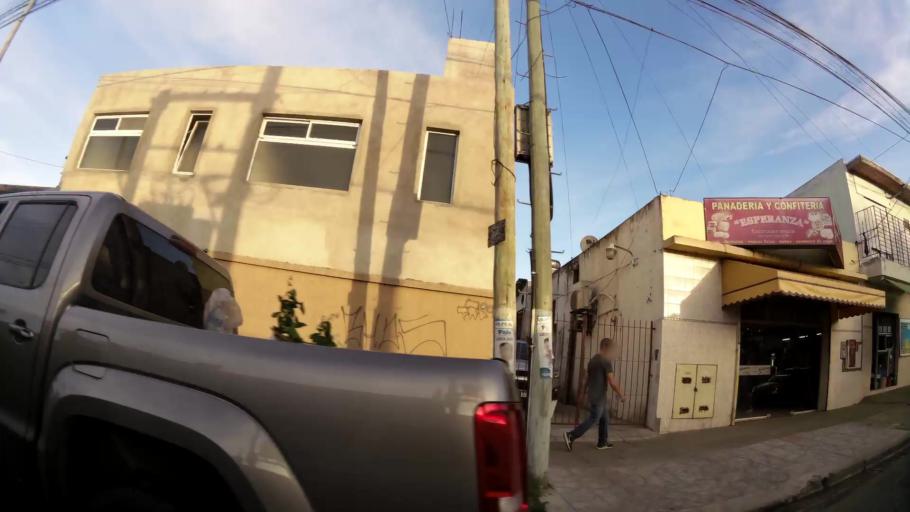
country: AR
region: Buenos Aires
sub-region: Partido de Quilmes
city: Quilmes
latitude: -34.7770
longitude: -58.1985
